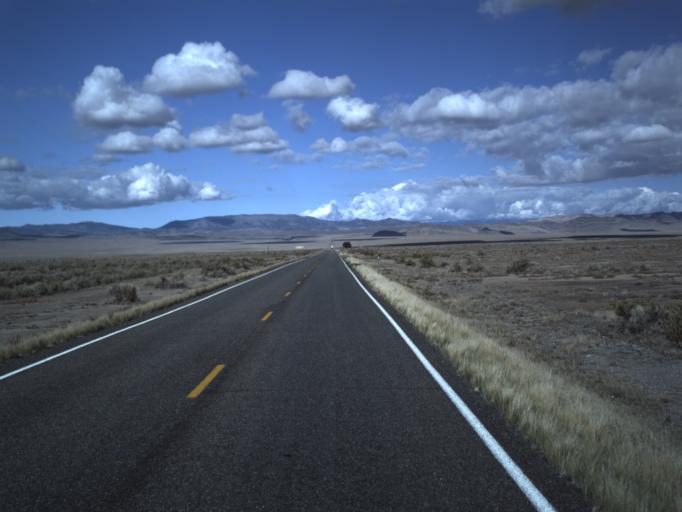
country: US
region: Utah
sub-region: Beaver County
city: Milford
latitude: 38.5282
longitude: -113.6707
